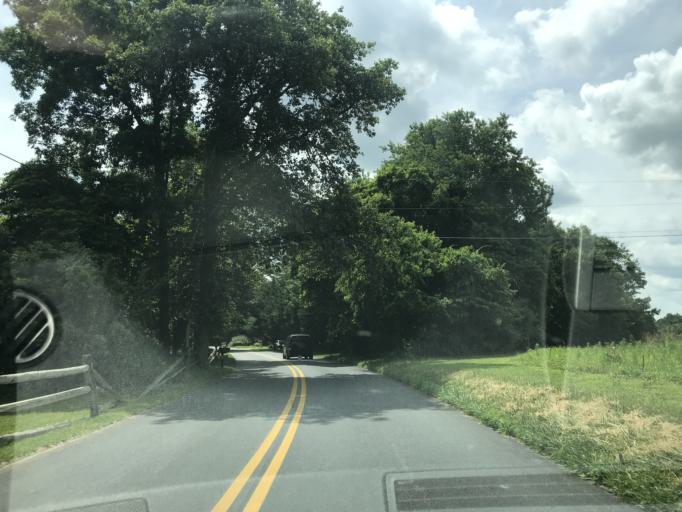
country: US
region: Maryland
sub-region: Carroll County
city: Hampstead
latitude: 39.6390
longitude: -76.8087
